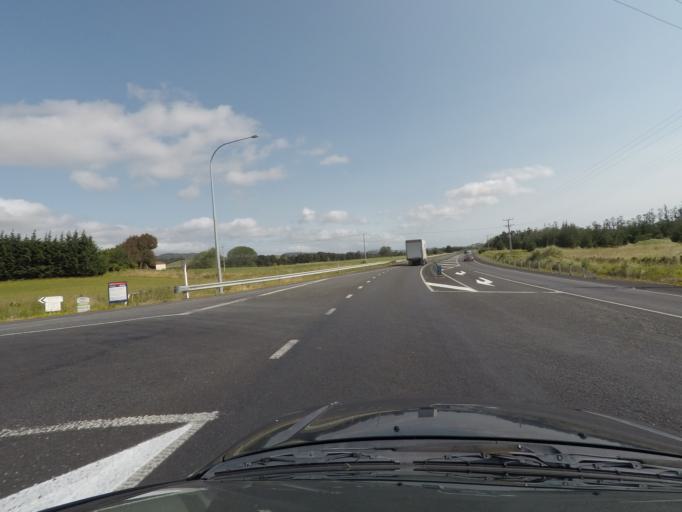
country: NZ
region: Northland
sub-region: Whangarei
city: Ruakaka
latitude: -36.0329
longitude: 174.4146
